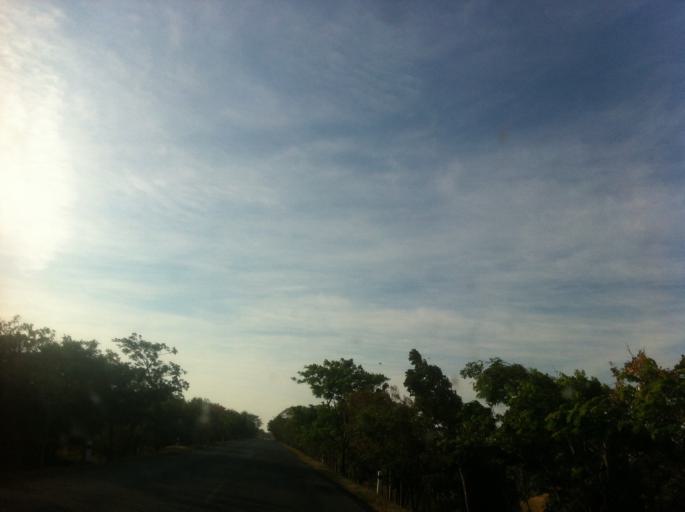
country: NI
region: Rivas
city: Rivas
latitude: 11.3376
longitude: -85.7288
